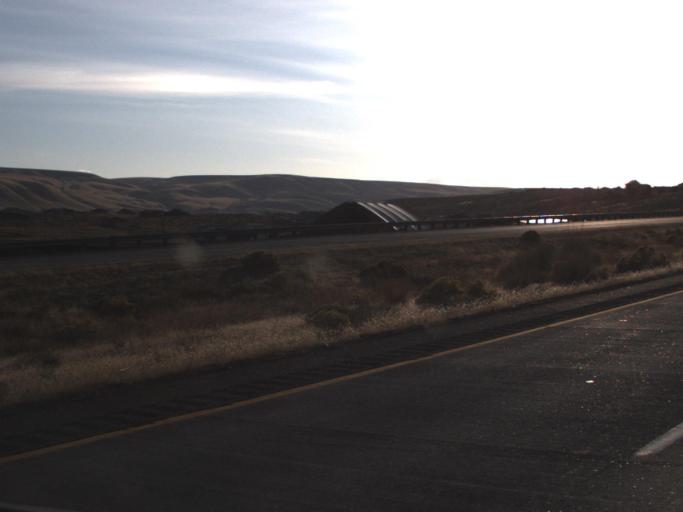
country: US
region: Washington
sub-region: Benton County
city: Richland
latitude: 46.1978
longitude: -119.2812
